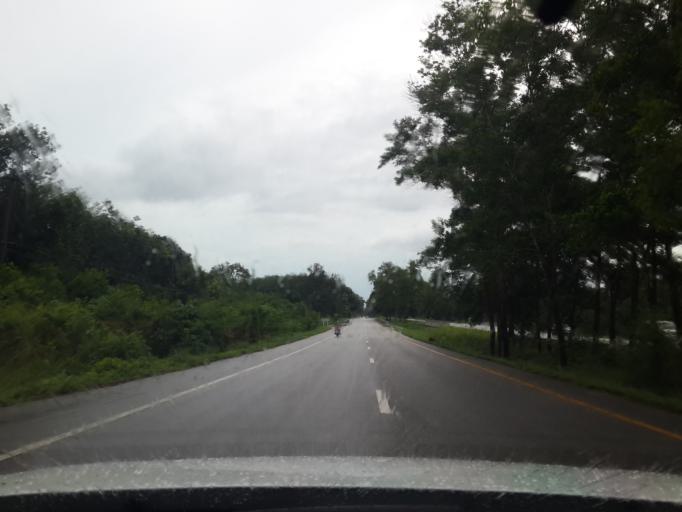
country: TH
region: Songkhla
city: Na Mom
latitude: 6.9870
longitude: 100.6503
